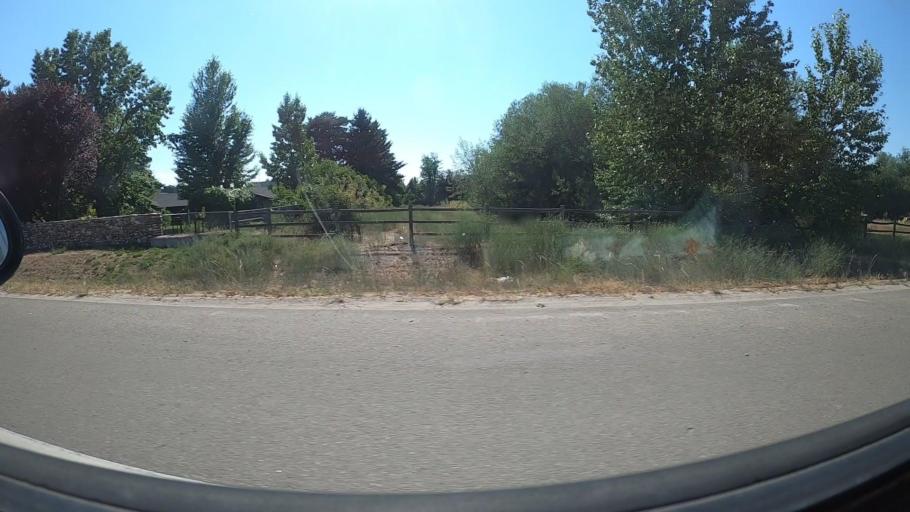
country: US
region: Idaho
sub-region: Ada County
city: Eagle
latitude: 43.6705
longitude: -116.3545
